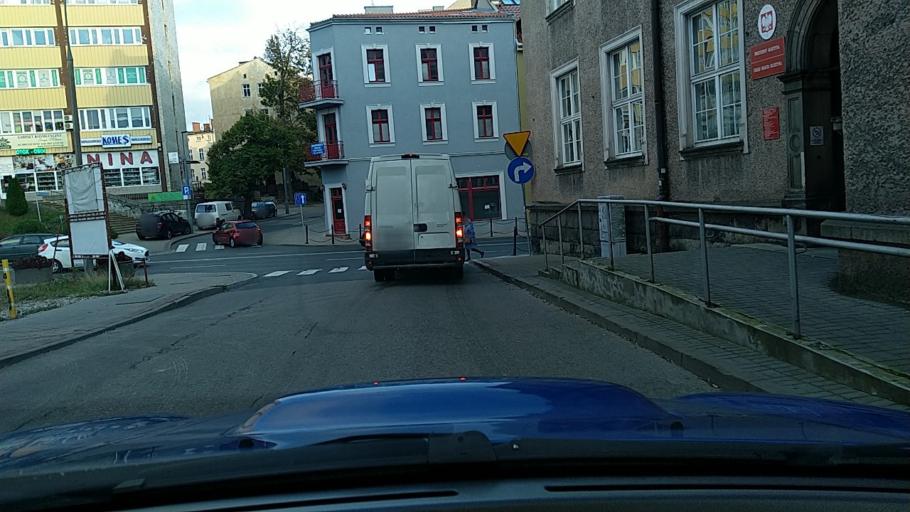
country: PL
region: Warmian-Masurian Voivodeship
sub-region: Powiat olsztynski
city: Olsztyn
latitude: 53.7794
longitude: 20.4797
